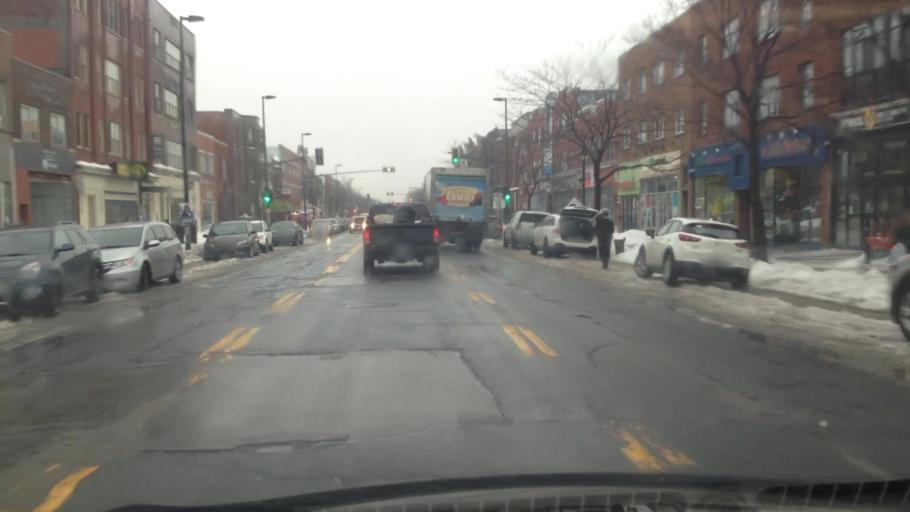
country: CA
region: Quebec
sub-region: Montreal
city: Montreal
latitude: 45.5225
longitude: -73.6030
